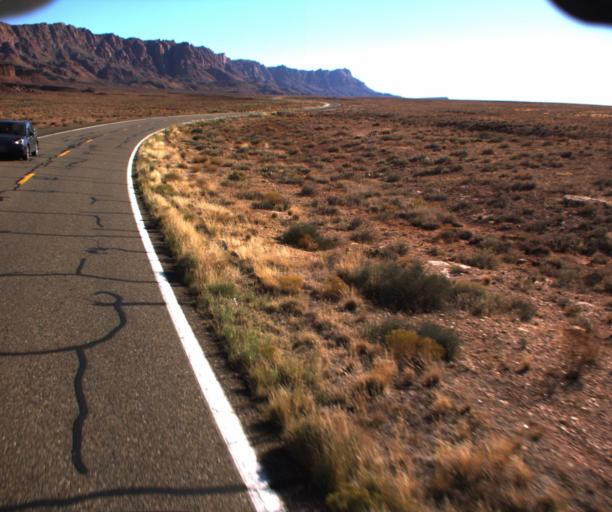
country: US
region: Arizona
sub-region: Coconino County
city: LeChee
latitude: 36.8029
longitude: -111.6116
